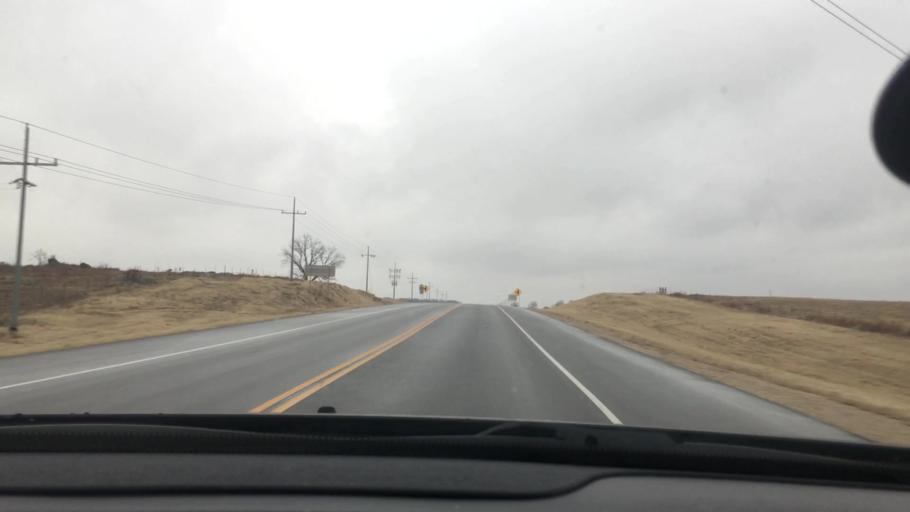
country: US
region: Oklahoma
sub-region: Johnston County
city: Tishomingo
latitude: 34.3666
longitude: -96.6360
